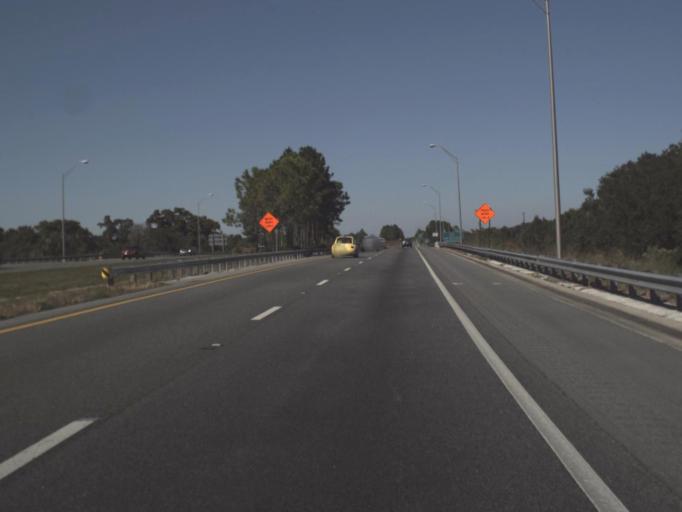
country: US
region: Florida
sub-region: Seminole County
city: Sanford
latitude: 28.7507
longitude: -81.2660
